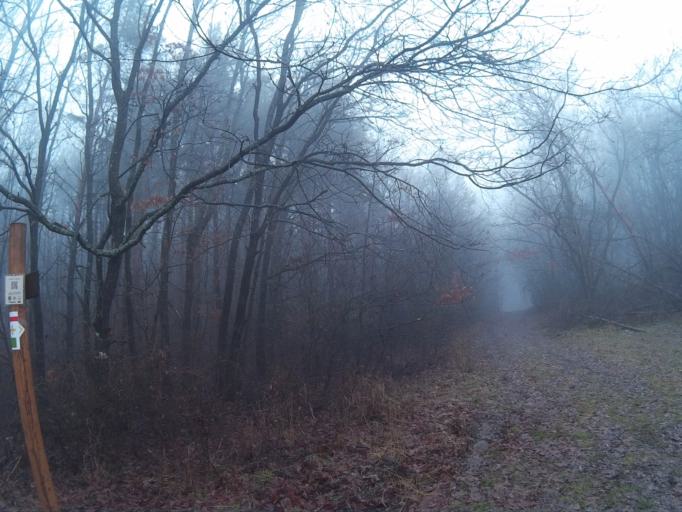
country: HU
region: Nograd
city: Somoskoujfalu
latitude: 48.1452
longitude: 19.8426
